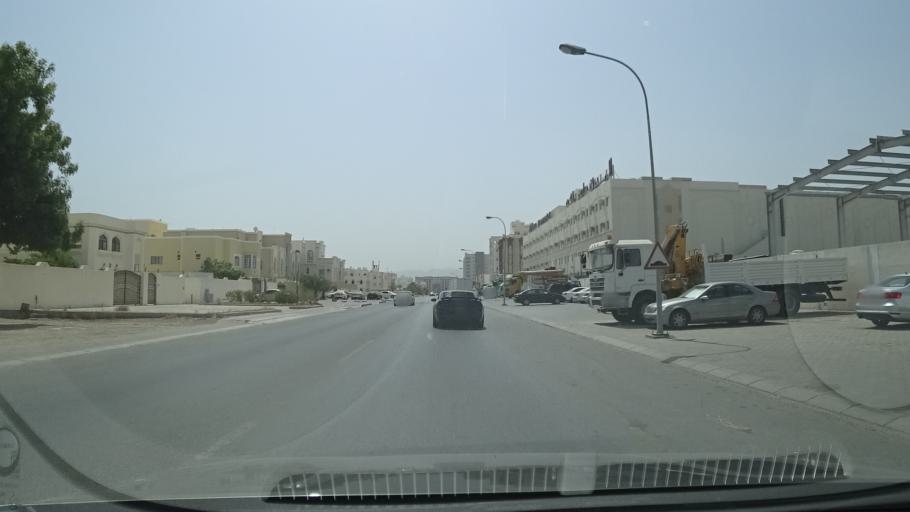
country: OM
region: Muhafazat Masqat
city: Bawshar
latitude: 23.5919
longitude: 58.3758
